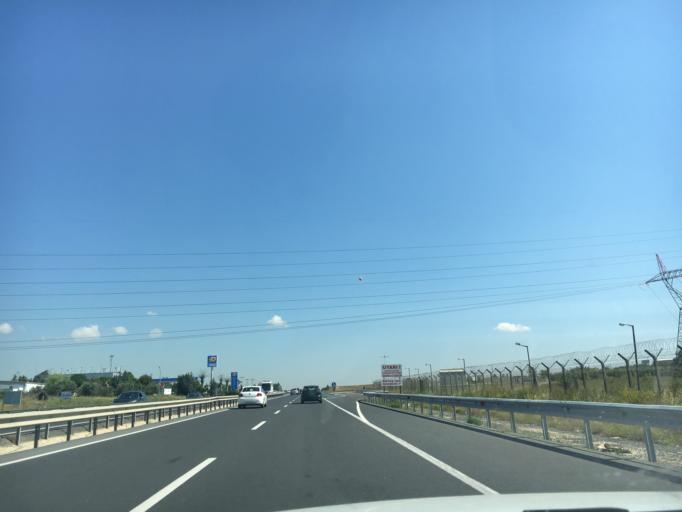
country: TR
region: Tekirdag
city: Sultankoy
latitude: 40.9949
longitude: 27.9733
